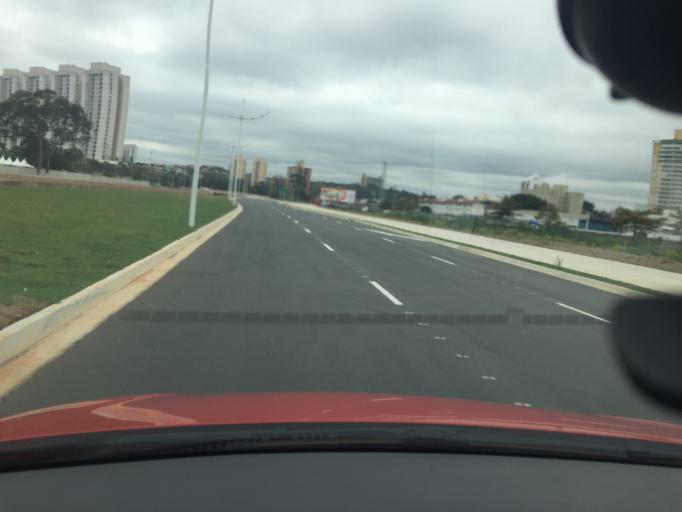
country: BR
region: Sao Paulo
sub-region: Jundiai
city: Jundiai
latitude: -23.1853
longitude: -46.9056
